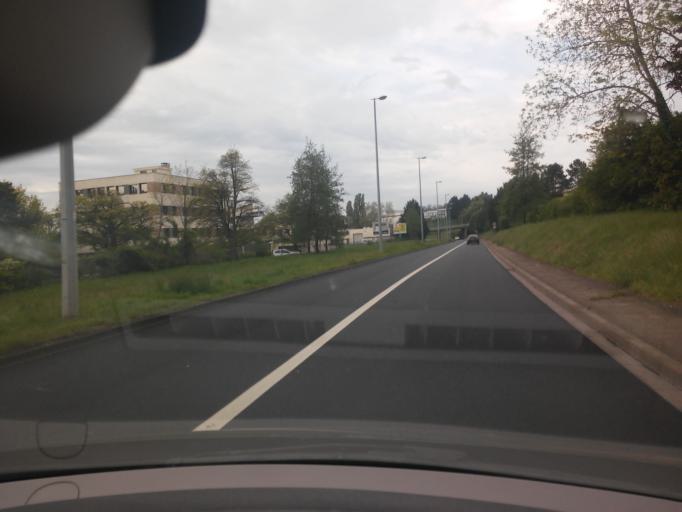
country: FR
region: Lorraine
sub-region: Departement de Meurthe-et-Moselle
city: Laxou
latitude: 48.6974
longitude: 6.1349
